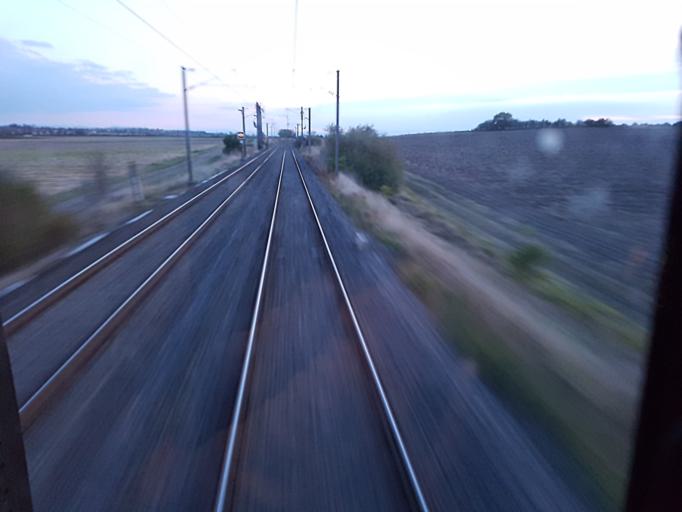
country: FR
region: Auvergne
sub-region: Departement du Puy-de-Dome
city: Randan
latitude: 45.9929
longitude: 3.3241
